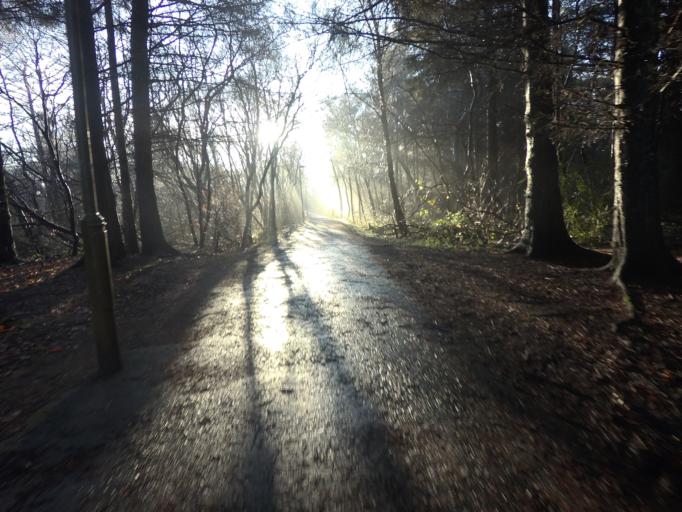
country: GB
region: Scotland
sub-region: West Lothian
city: Livingston
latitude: 55.9071
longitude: -3.5285
